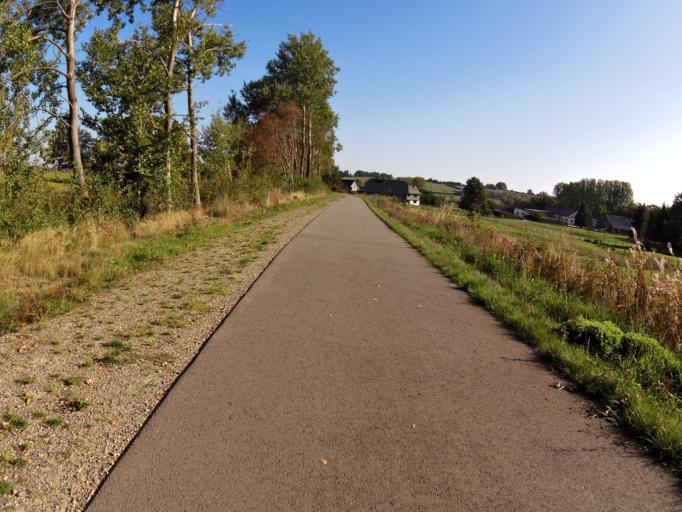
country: BE
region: Wallonia
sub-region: Province de Liege
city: Ambleve
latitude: 50.3359
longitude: 6.1182
